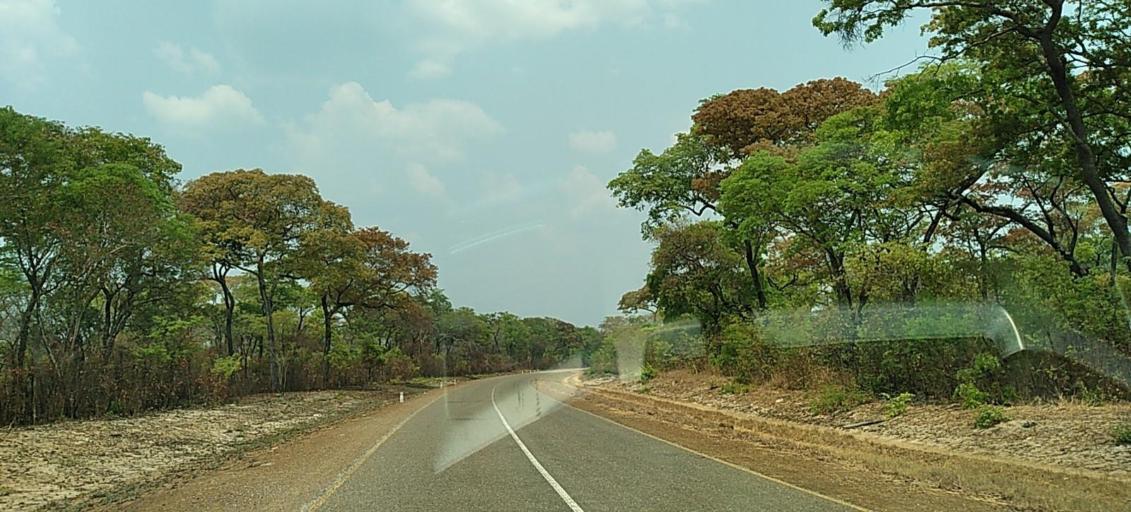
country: ZM
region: North-Western
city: Zambezi
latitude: -13.5583
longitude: 23.2081
